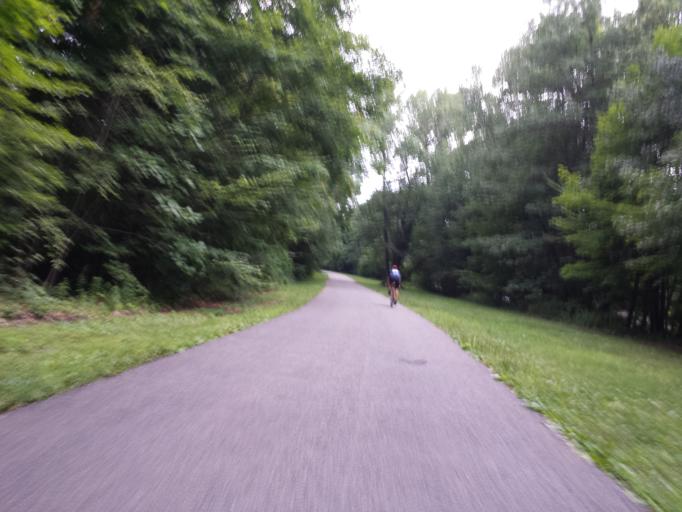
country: US
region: New York
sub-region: Ulster County
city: Highland
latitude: 41.7297
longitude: -73.9713
